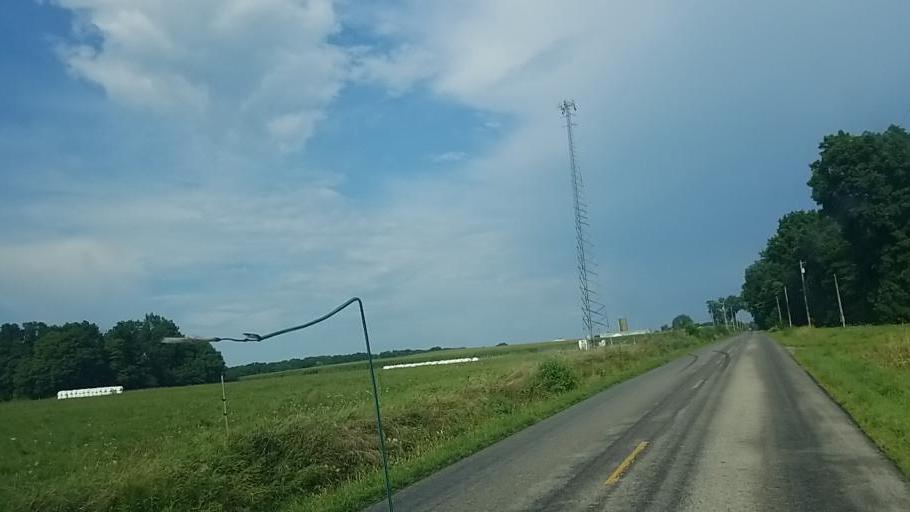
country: US
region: Ohio
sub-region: Wayne County
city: Creston
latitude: 40.9155
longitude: -81.9345
